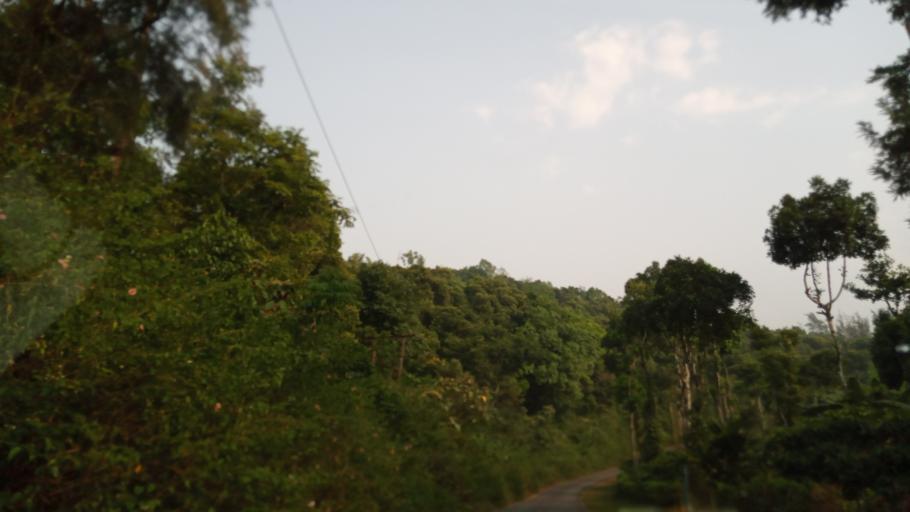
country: IN
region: Karnataka
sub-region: Chikmagalur
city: Mudigere
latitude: 13.0115
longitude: 75.6285
